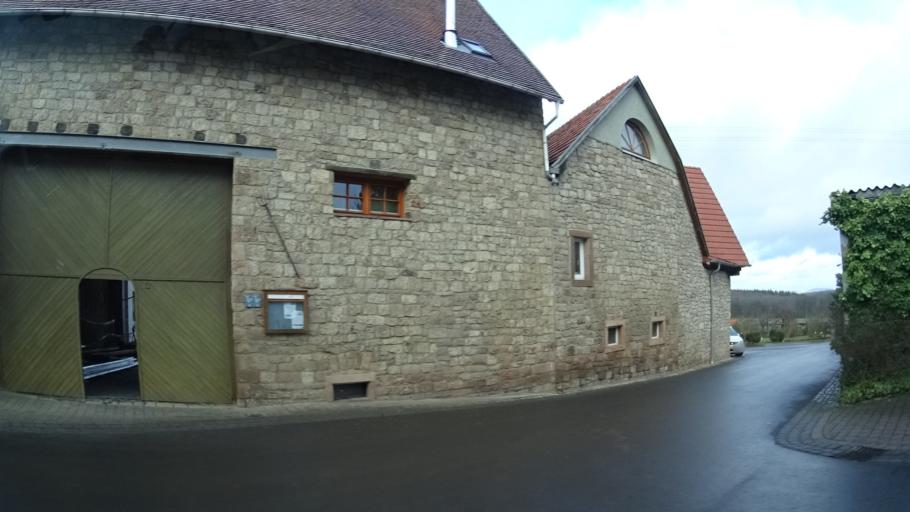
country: DE
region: Rheinland-Pfalz
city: Sankt Alban
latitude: 49.6860
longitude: 7.8879
